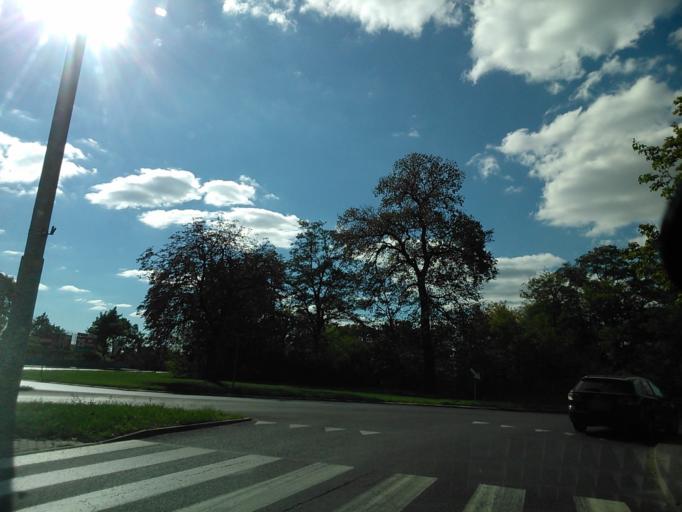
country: PL
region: Kujawsko-Pomorskie
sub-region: Torun
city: Torun
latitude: 53.0157
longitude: 18.6192
